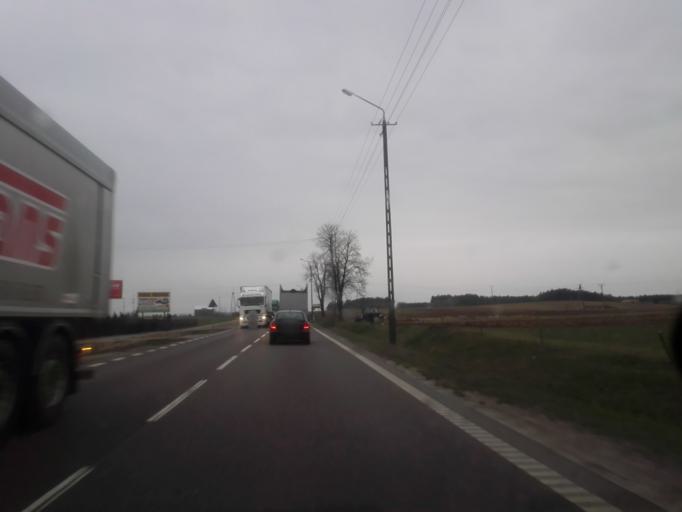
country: PL
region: Podlasie
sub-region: Powiat grajewski
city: Grajewo
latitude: 53.6205
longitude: 22.3968
